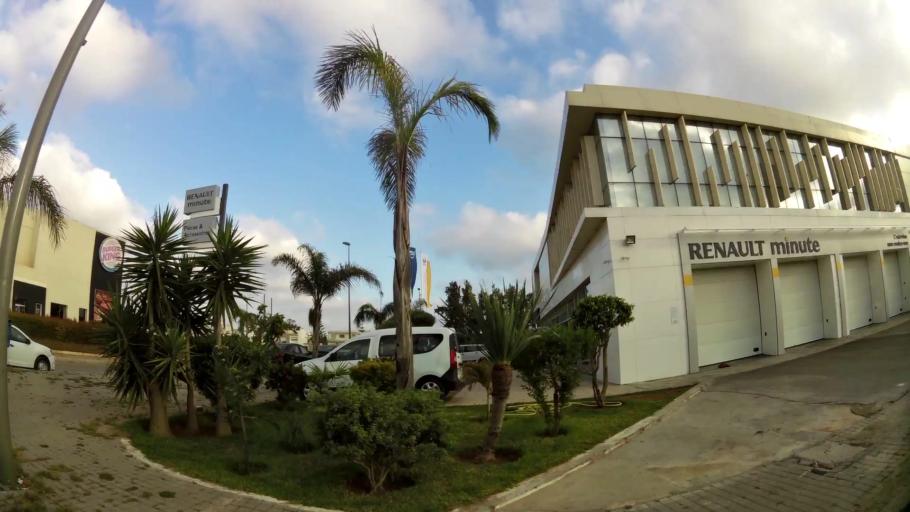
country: MA
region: Rabat-Sale-Zemmour-Zaer
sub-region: Rabat
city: Rabat
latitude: 33.9560
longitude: -6.8417
